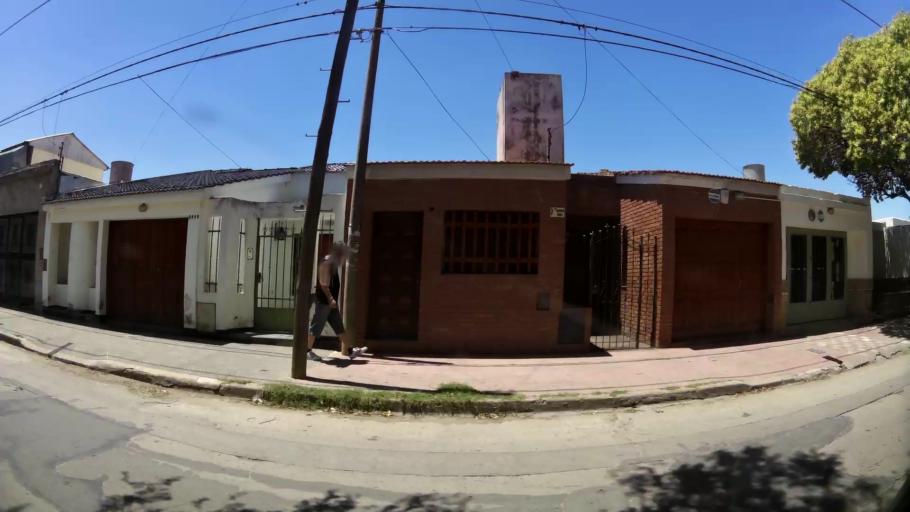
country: AR
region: Cordoba
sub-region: Departamento de Capital
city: Cordoba
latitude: -31.3849
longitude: -64.1372
